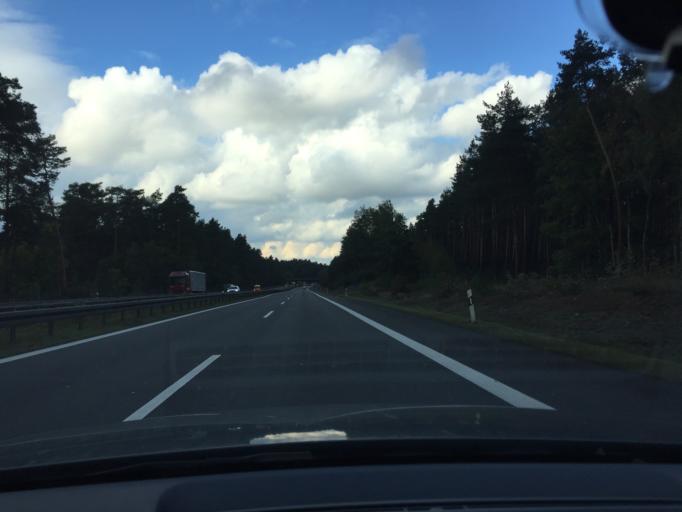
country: DE
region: Brandenburg
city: Bronkow
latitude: 51.7331
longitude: 13.8701
